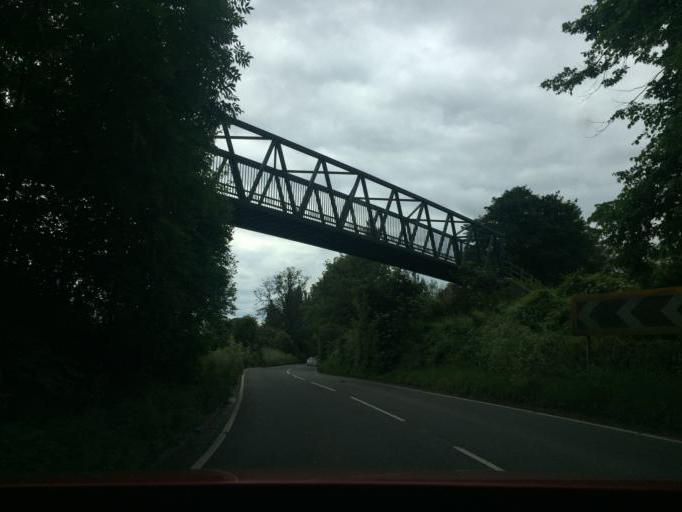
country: GB
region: England
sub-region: Hertfordshire
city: Harpenden
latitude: 51.8529
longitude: -0.3769
